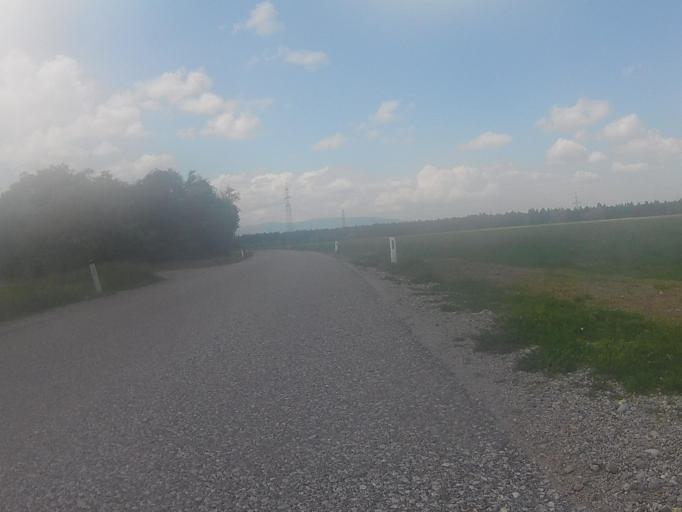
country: SI
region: Kidricevo
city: Kidricevo
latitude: 46.4258
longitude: 15.7794
